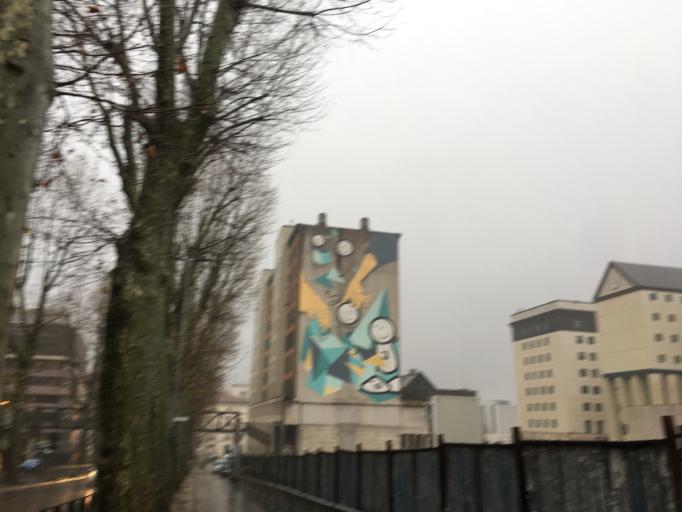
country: IT
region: Umbria
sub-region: Provincia di Perugia
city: Perugia
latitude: 43.1054
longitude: 12.3779
